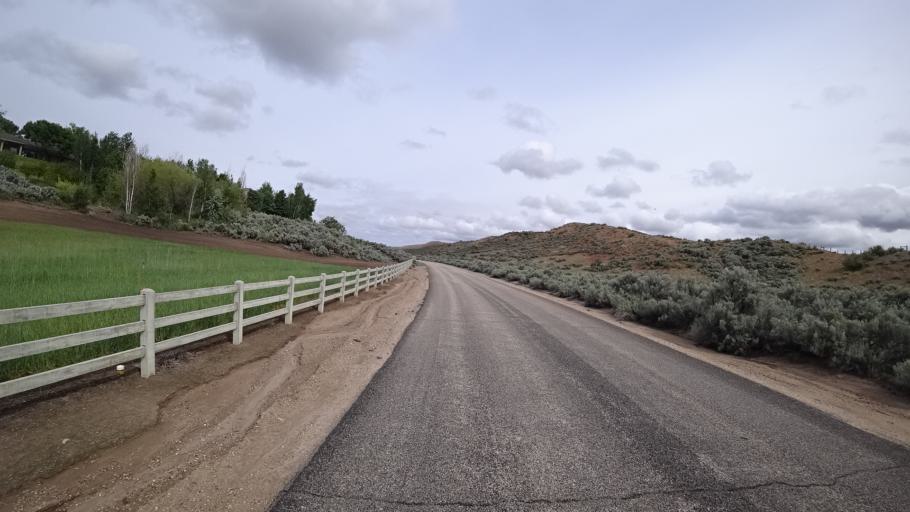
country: US
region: Idaho
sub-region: Ada County
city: Eagle
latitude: 43.7489
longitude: -116.3577
